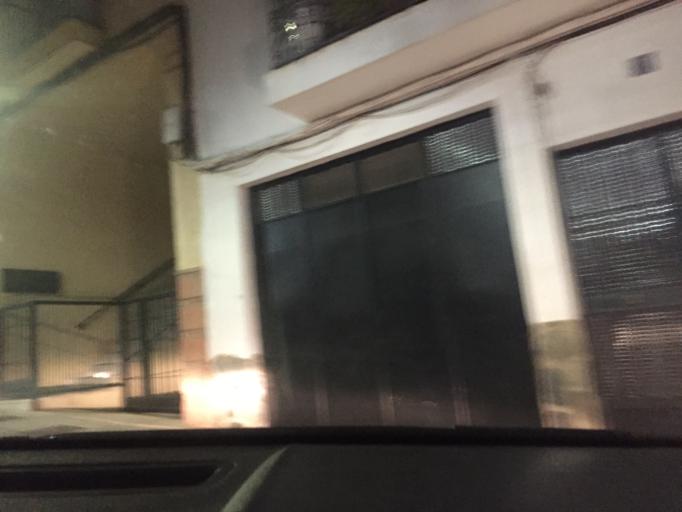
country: ES
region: Andalusia
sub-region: Provincia de Jaen
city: Jaen
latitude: 37.7676
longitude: -3.7814
